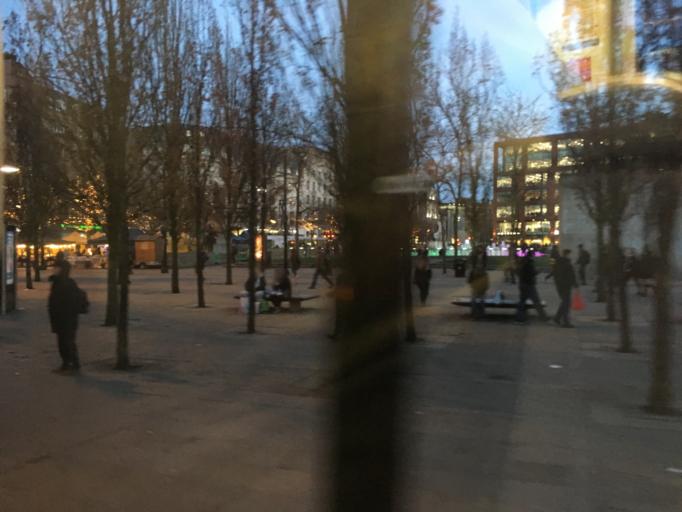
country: GB
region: England
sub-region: Manchester
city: Manchester
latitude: 53.4814
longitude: -2.2381
